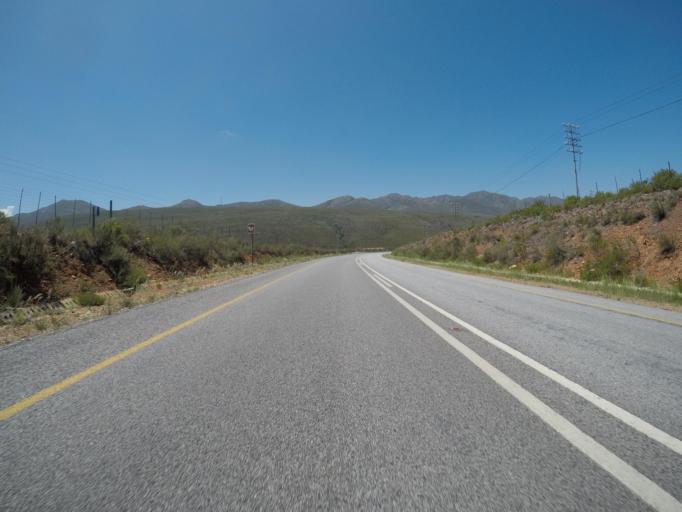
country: ZA
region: Eastern Cape
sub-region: Cacadu District Municipality
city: Kareedouw
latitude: -33.9441
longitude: 24.3057
